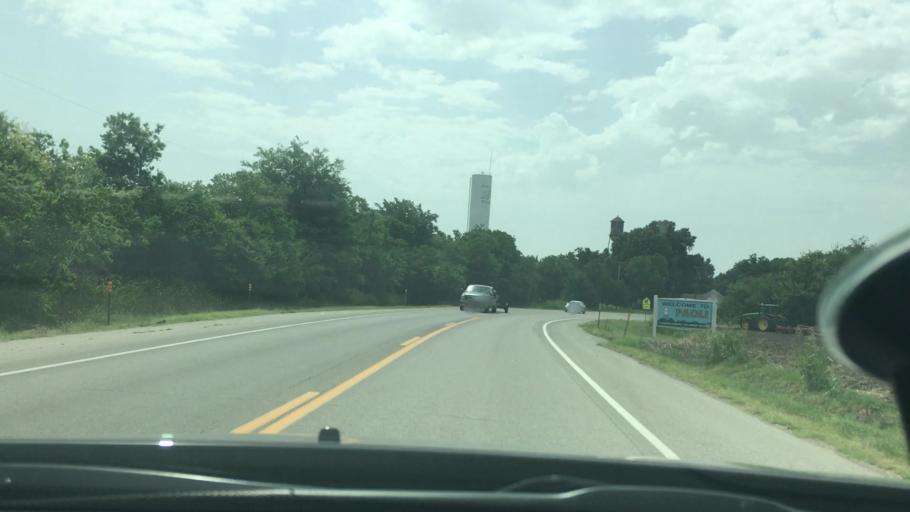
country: US
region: Oklahoma
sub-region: Garvin County
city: Pauls Valley
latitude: 34.8309
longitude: -97.2606
